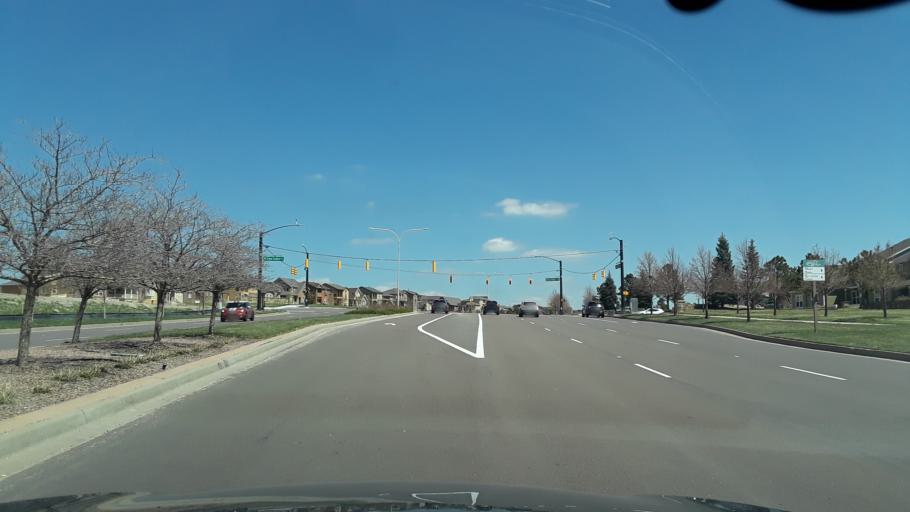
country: US
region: Colorado
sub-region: El Paso County
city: Black Forest
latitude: 38.9576
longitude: -104.7259
